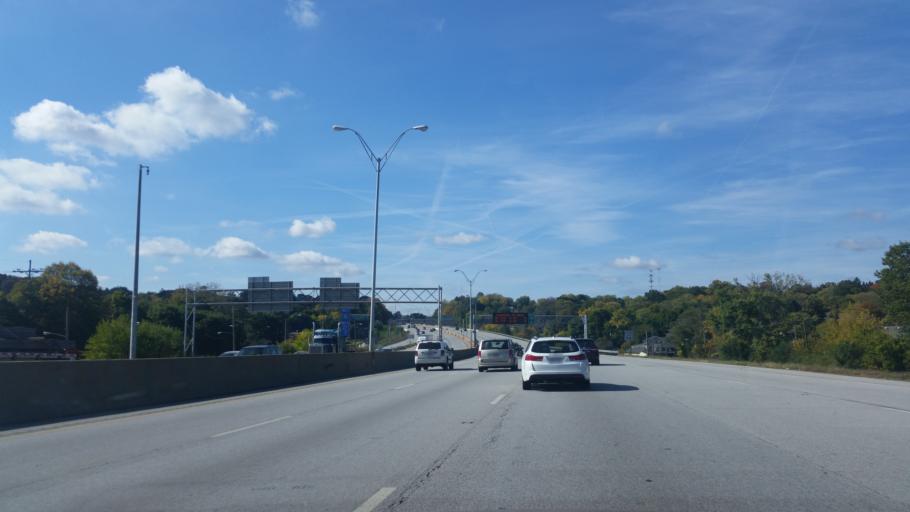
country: US
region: Ohio
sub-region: Summit County
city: Akron
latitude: 41.0621
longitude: -81.5445
